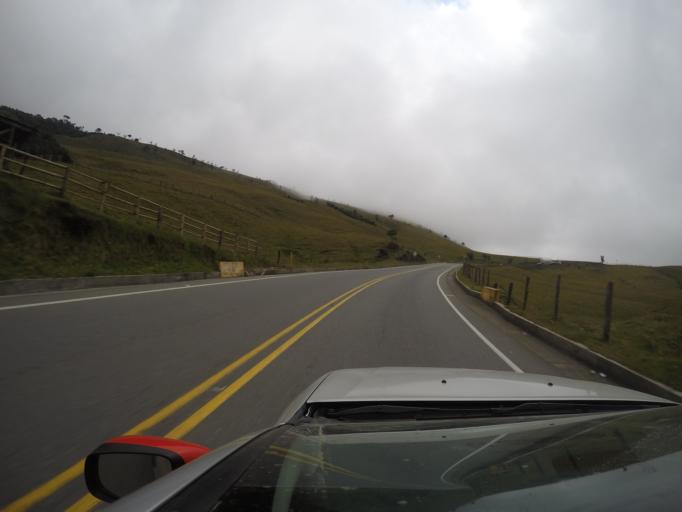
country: CO
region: Tolima
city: Herveo
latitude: 5.0402
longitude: -75.3354
